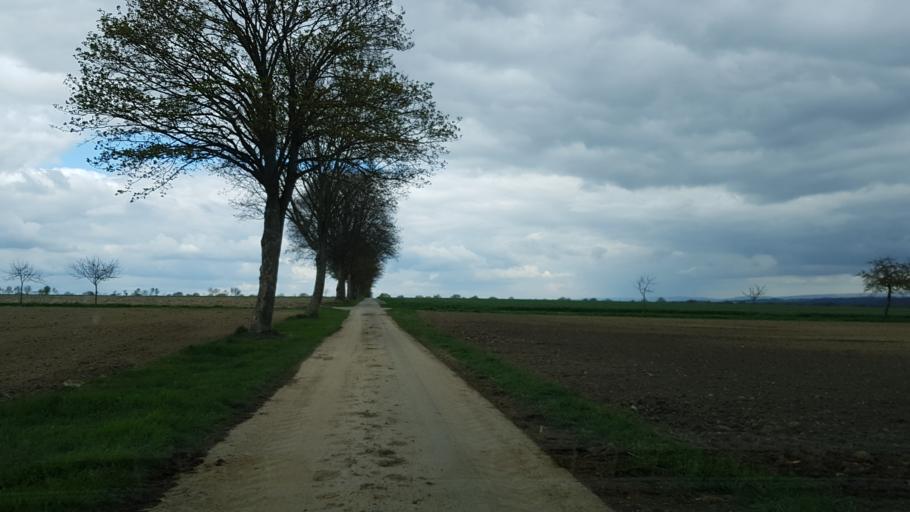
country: DE
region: North Rhine-Westphalia
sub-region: Regierungsbezirk Detmold
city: Wunnenberg
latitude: 51.6107
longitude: 8.7449
